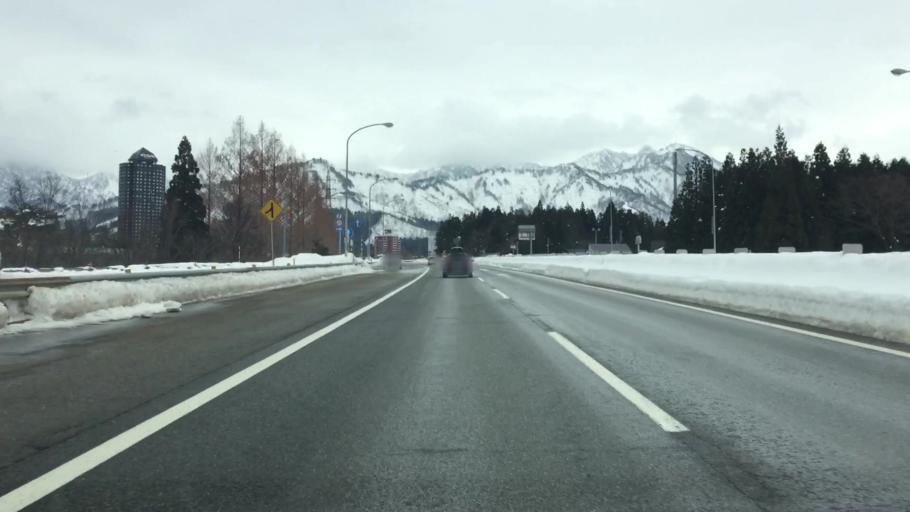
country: JP
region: Niigata
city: Shiozawa
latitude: 36.9326
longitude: 138.8292
